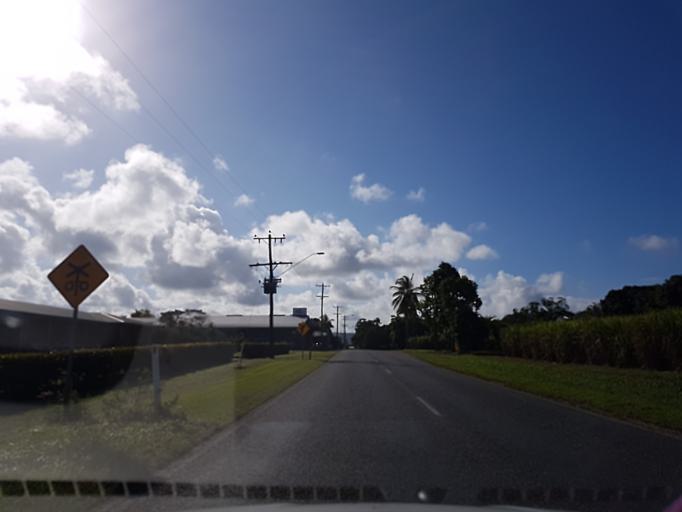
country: AU
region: Queensland
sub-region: Cairns
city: Port Douglas
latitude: -16.4025
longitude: 145.3815
